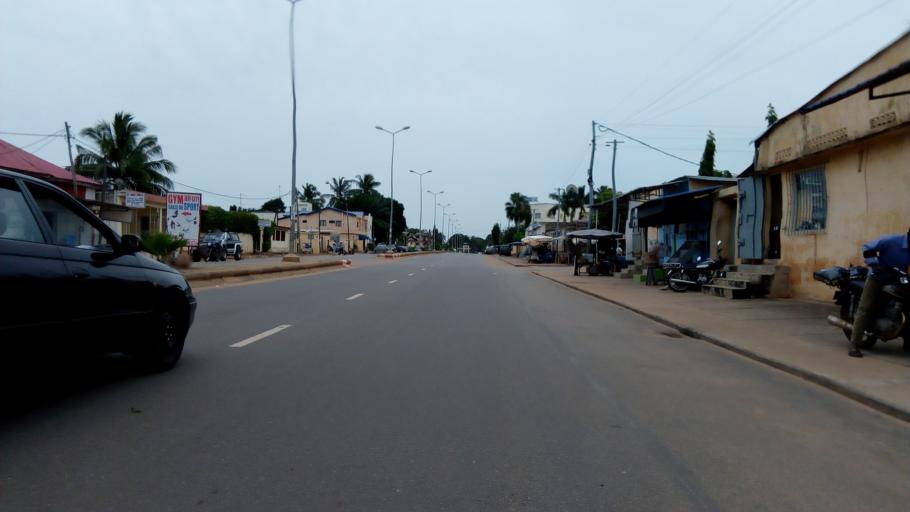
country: TG
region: Maritime
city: Lome
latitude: 6.1603
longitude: 1.2290
